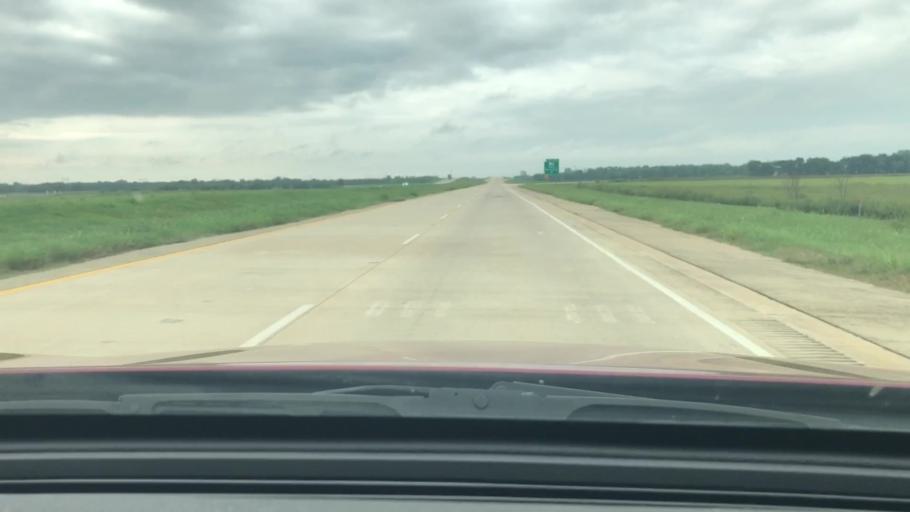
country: US
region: Louisiana
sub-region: Caddo Parish
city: Blanchard
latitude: 32.6806
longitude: -93.8530
